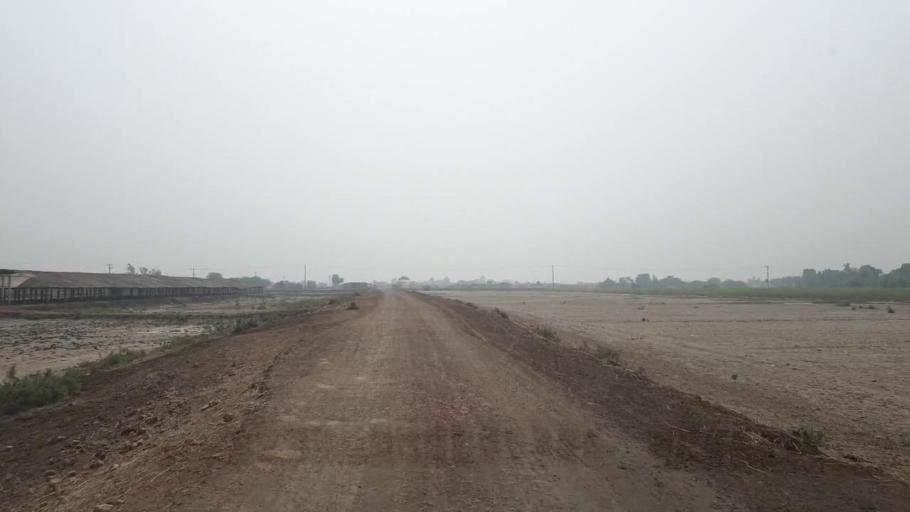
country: PK
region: Sindh
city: Kario
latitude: 24.6474
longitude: 68.6398
